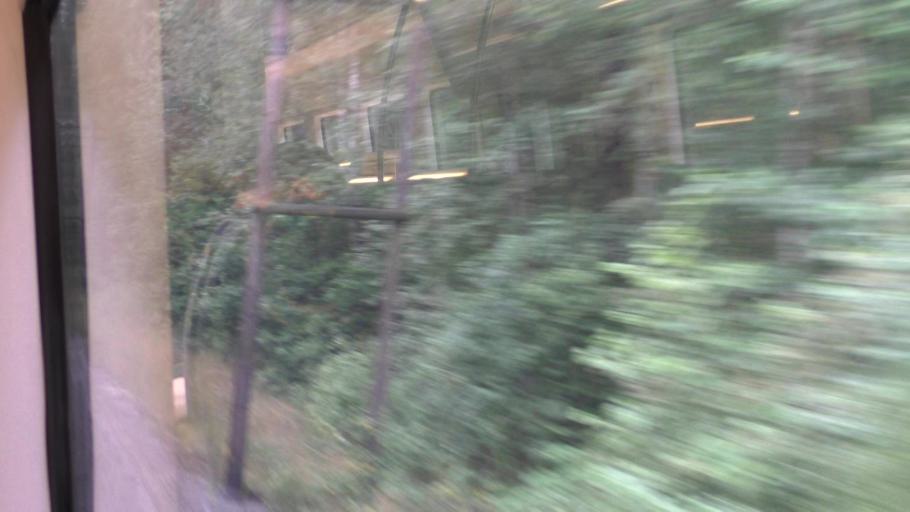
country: DE
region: Saxony
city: Horka
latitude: 51.2754
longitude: 14.9045
